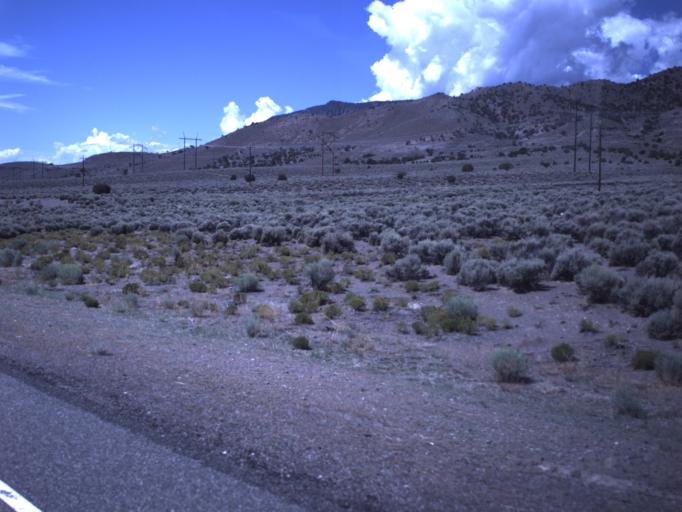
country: US
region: Utah
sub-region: Piute County
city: Junction
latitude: 38.3160
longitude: -112.2211
